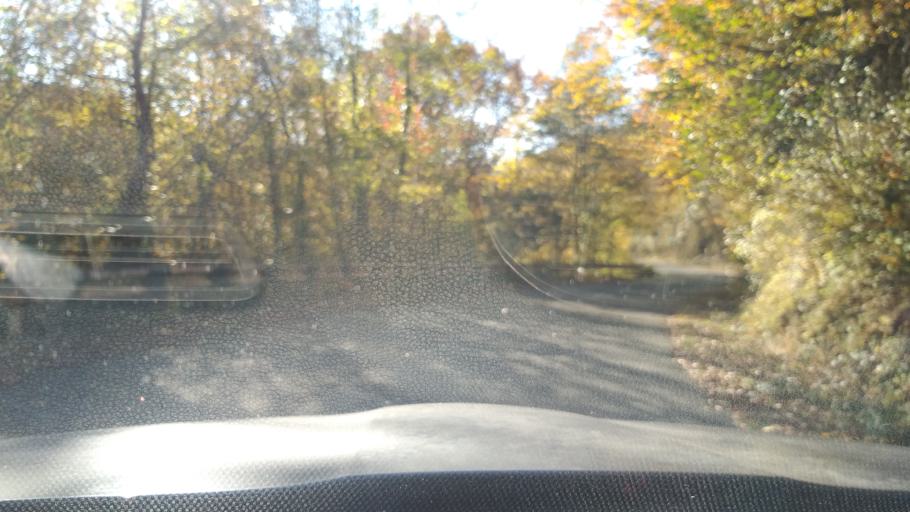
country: GE
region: Abkhazia
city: Bich'vinta
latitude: 43.1928
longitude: 40.4559
